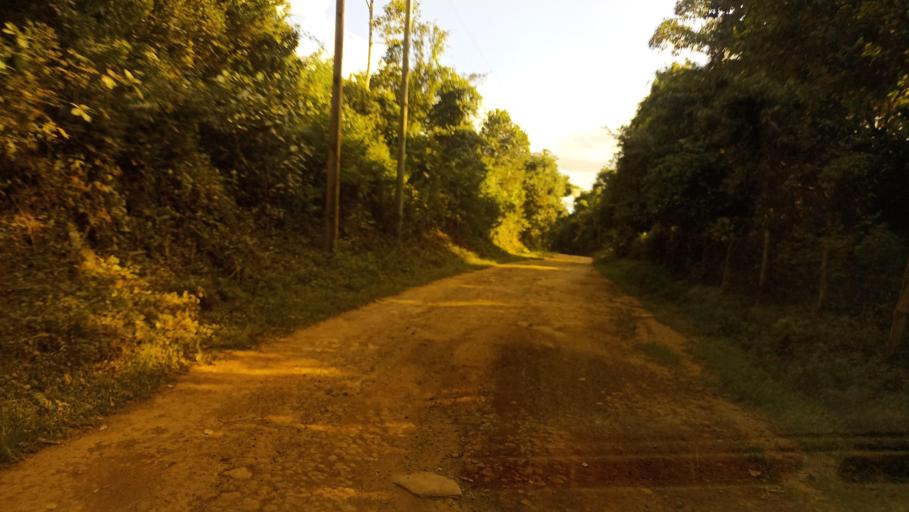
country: BR
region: Minas Gerais
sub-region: Ouro Preto
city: Ouro Preto
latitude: -20.3052
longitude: -43.5765
